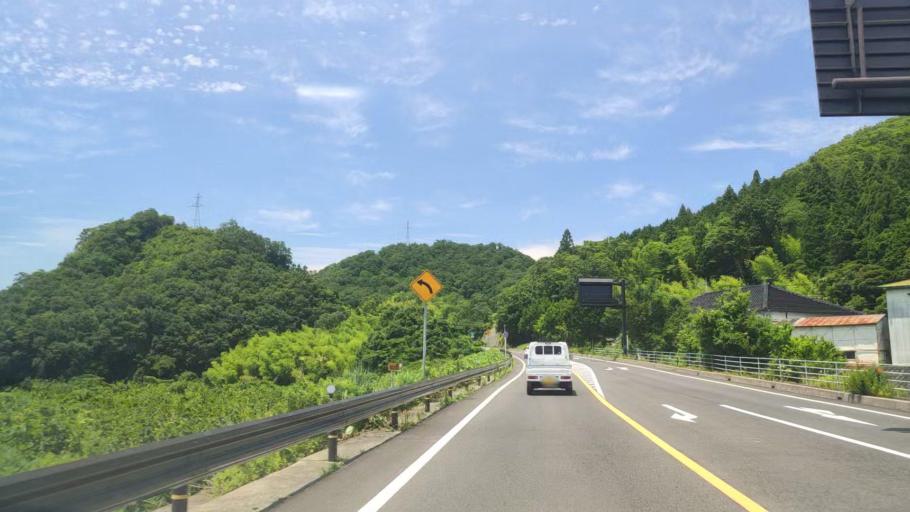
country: JP
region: Tottori
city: Tottori
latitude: 35.3986
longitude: 134.2682
